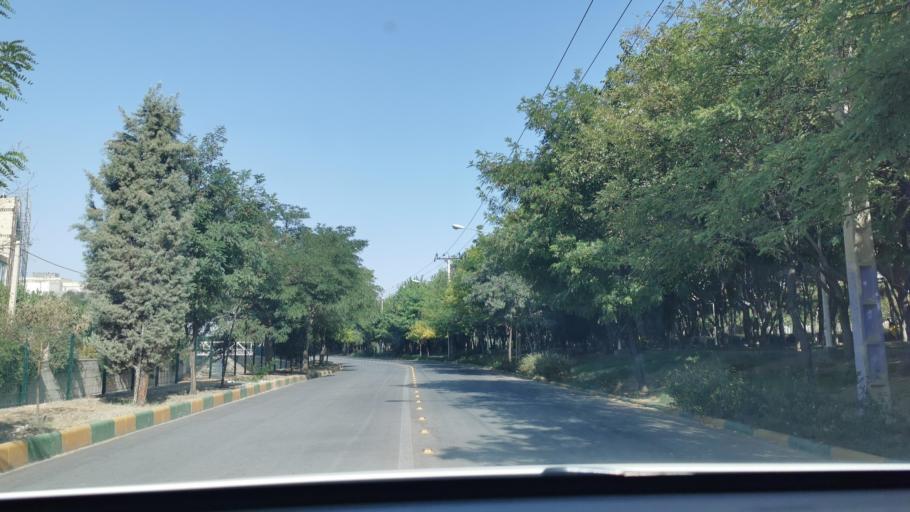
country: IR
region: Razavi Khorasan
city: Mashhad
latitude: 36.3298
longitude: 59.6351
